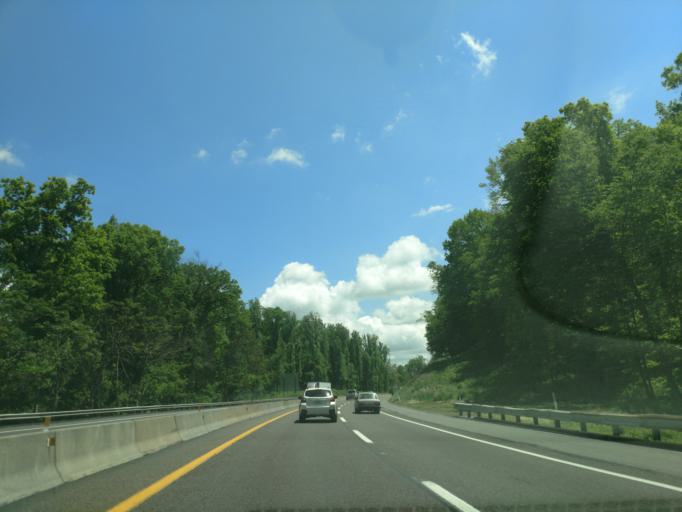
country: US
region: Pennsylvania
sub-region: Chester County
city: Elverson
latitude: 40.1157
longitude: -75.7638
